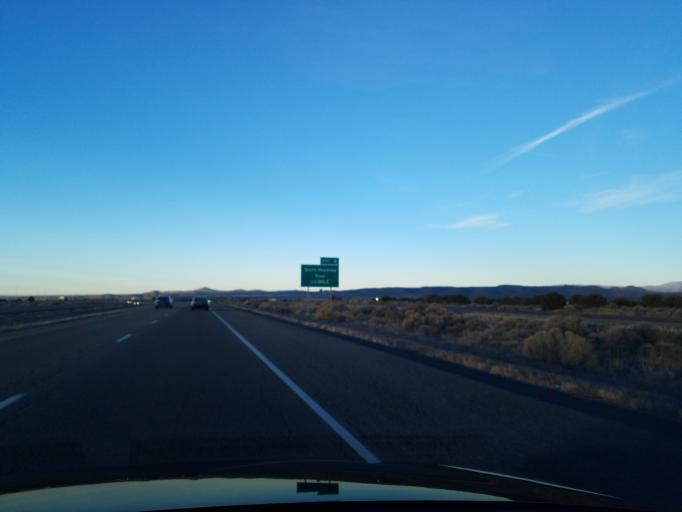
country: US
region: New Mexico
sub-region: Santa Fe County
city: Agua Fria
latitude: 35.6660
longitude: -106.0272
